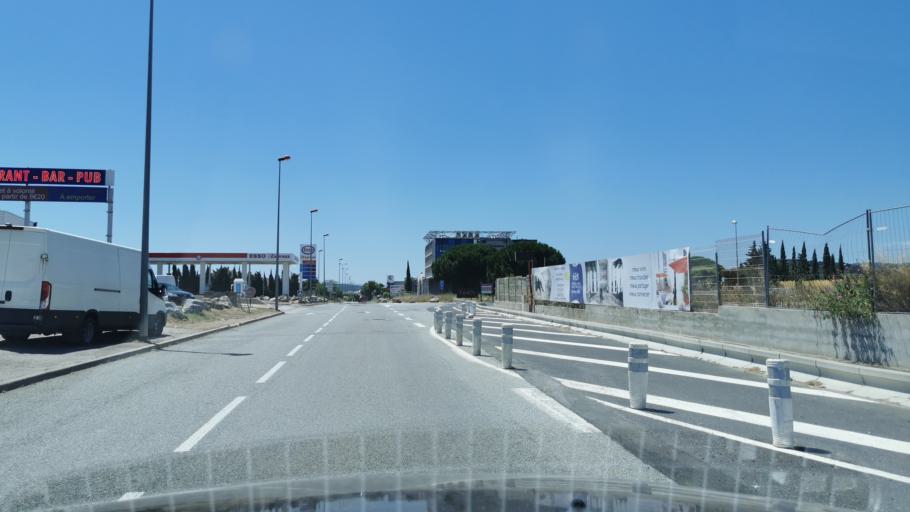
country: FR
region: Languedoc-Roussillon
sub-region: Departement de l'Aude
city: Narbonne
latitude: 43.1621
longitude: 2.9880
